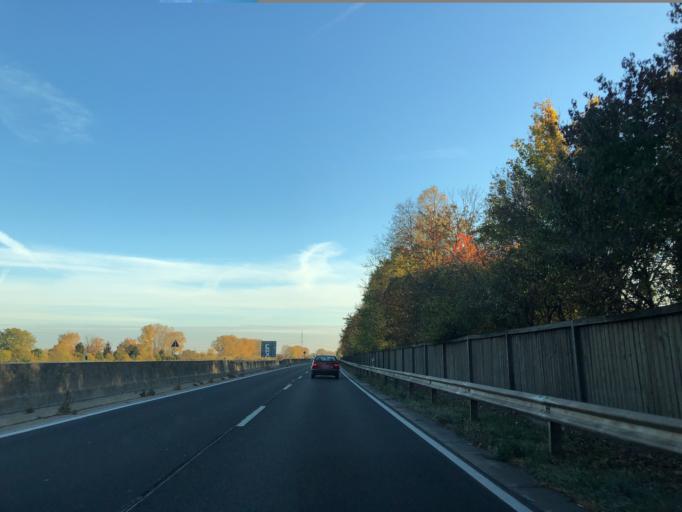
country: DE
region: Hesse
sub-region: Regierungsbezirk Darmstadt
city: Ginsheim-Gustavsburg
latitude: 49.9644
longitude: 8.3263
